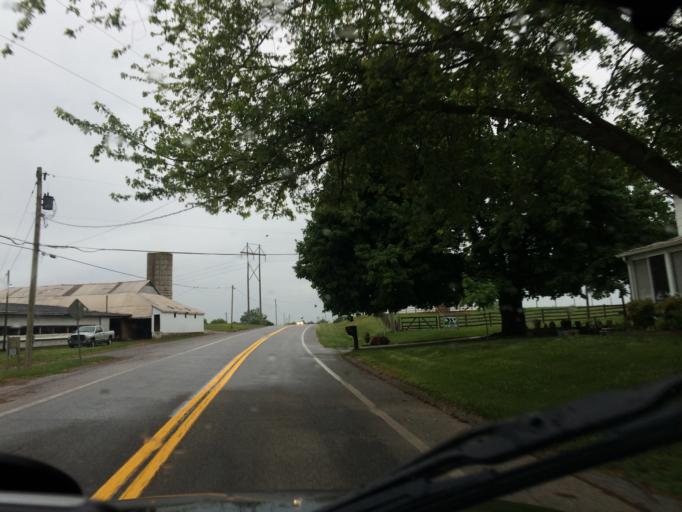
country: US
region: Maryland
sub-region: Carroll County
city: Taneytown
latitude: 39.5961
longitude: -77.1682
